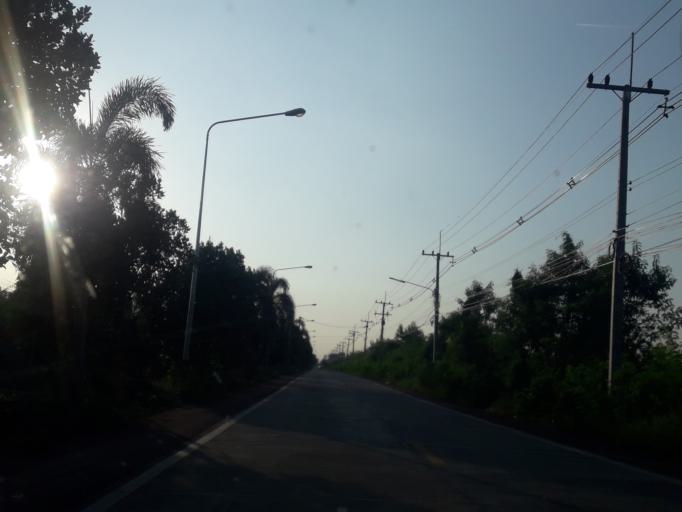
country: TH
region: Pathum Thani
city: Nong Suea
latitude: 14.1365
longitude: 100.8531
